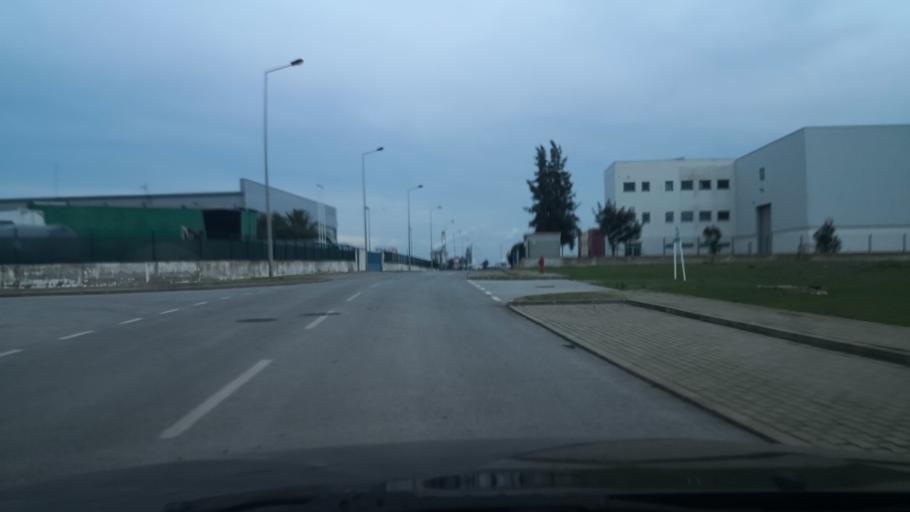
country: PT
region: Setubal
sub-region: Setubal
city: Setubal
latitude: 38.4984
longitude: -8.8276
